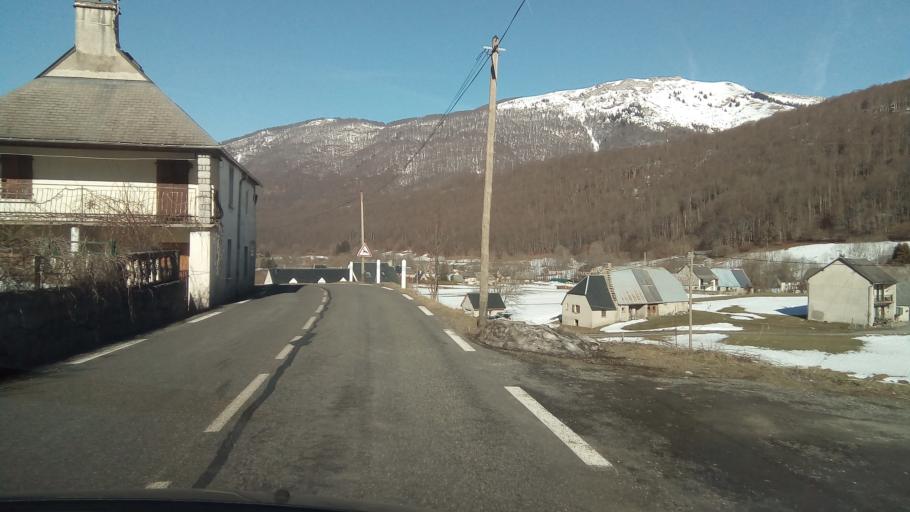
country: FR
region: Midi-Pyrenees
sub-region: Departement des Hautes-Pyrenees
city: Campan
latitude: 42.9596
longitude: 0.2310
